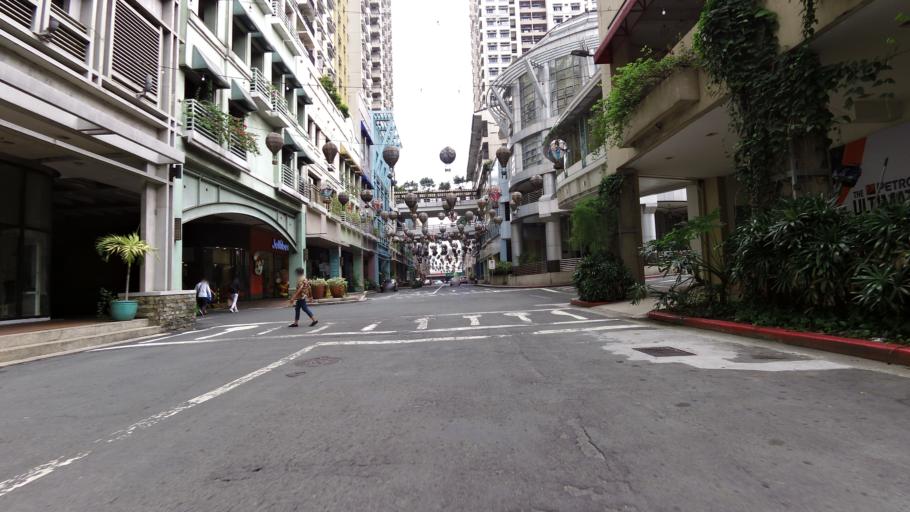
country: PH
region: Metro Manila
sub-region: Quezon City
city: Quezon City
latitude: 14.6227
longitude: 121.0539
